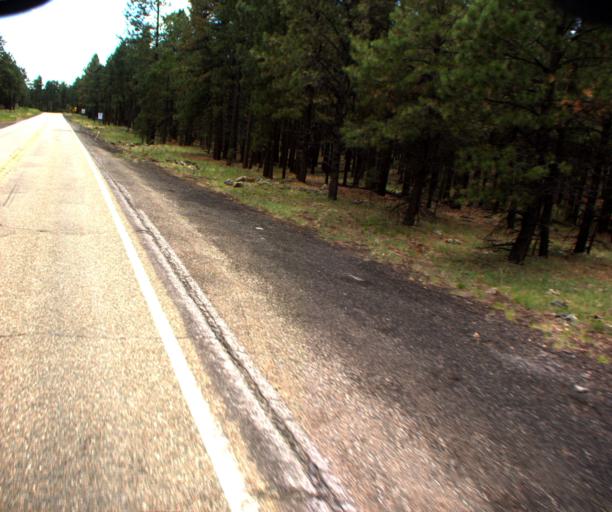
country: US
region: Arizona
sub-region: Coconino County
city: Flagstaff
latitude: 35.3132
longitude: -111.7752
